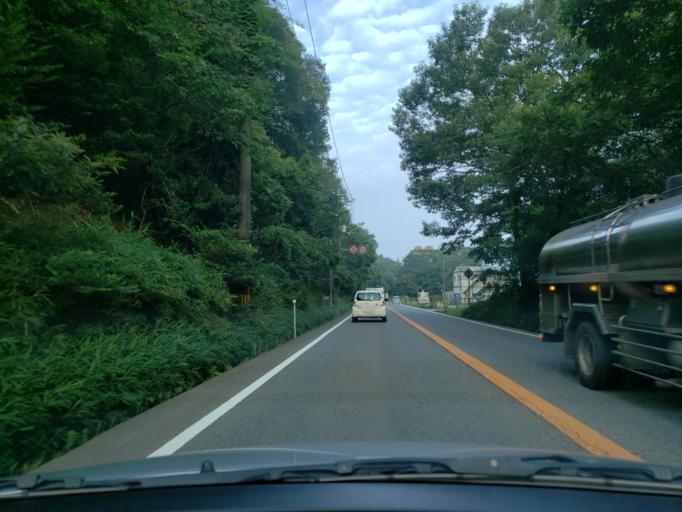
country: JP
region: Hyogo
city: Aioi
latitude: 34.8312
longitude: 134.4100
